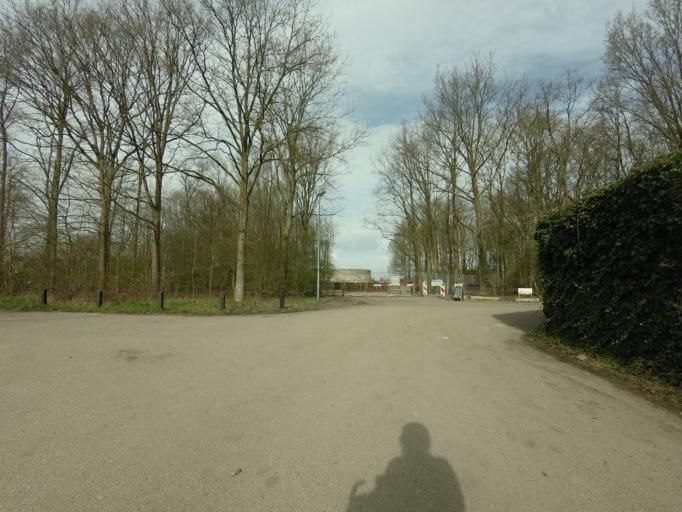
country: NL
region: North Holland
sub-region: Gemeente Weesp
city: Weesp
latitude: 52.2927
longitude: 5.0834
